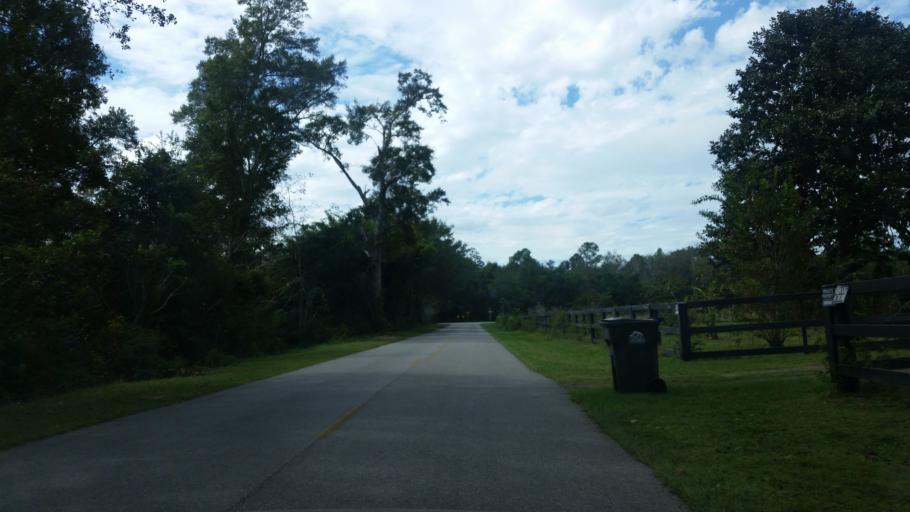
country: US
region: Florida
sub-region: Santa Rosa County
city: Point Baker
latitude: 30.7335
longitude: -87.0417
